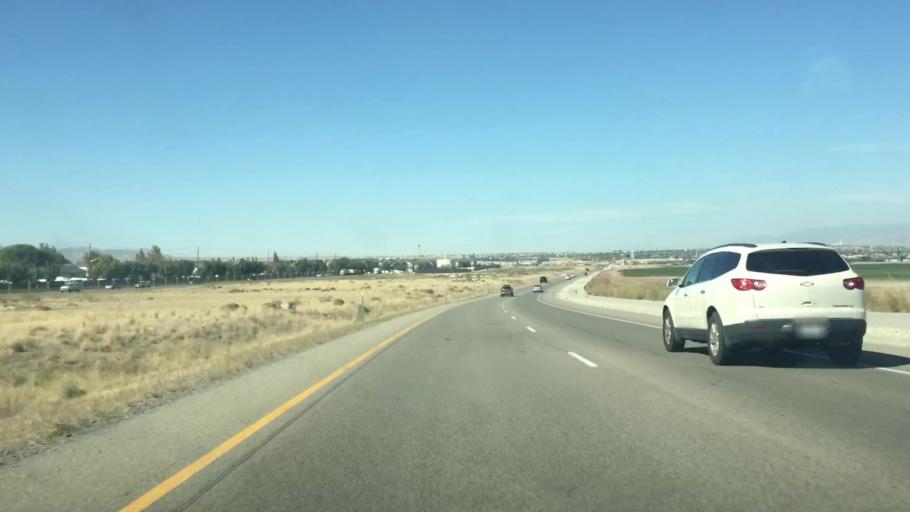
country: US
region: Utah
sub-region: Salt Lake County
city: Herriman
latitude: 40.4949
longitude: -112.0011
